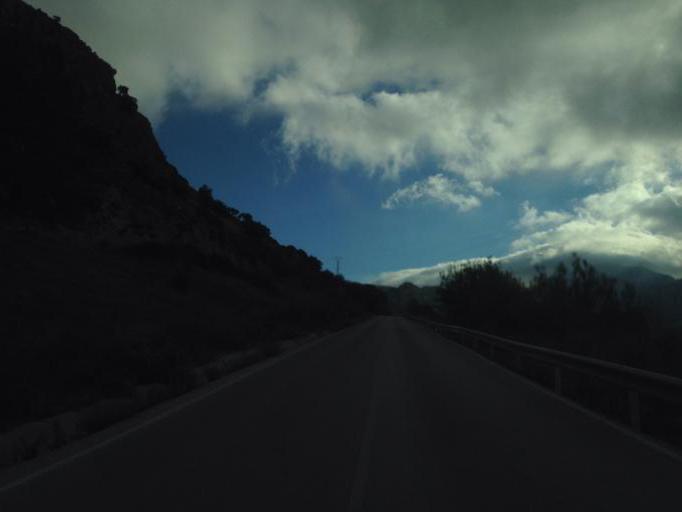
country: ES
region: Andalusia
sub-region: Provincia de Malaga
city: Casabermeja
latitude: 36.9561
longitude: -4.4362
